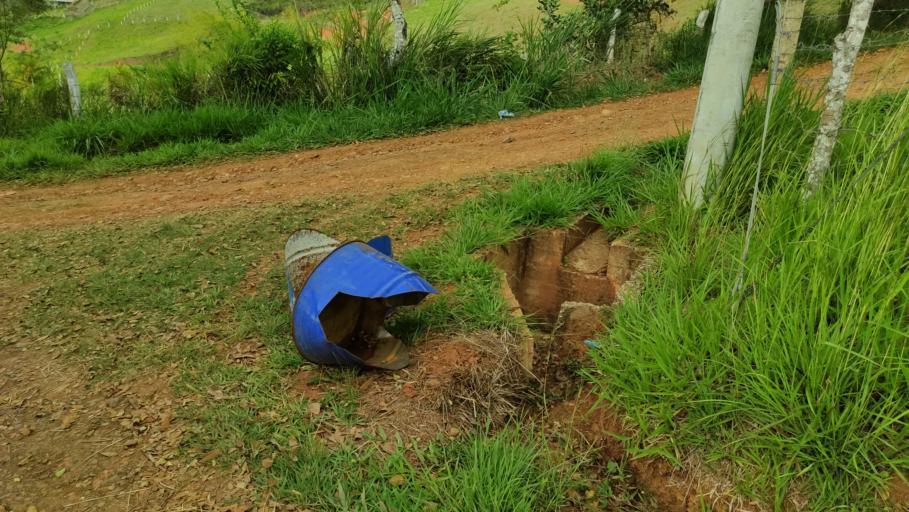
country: CO
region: Valle del Cauca
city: Dagua
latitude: 3.5395
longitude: -76.6438
